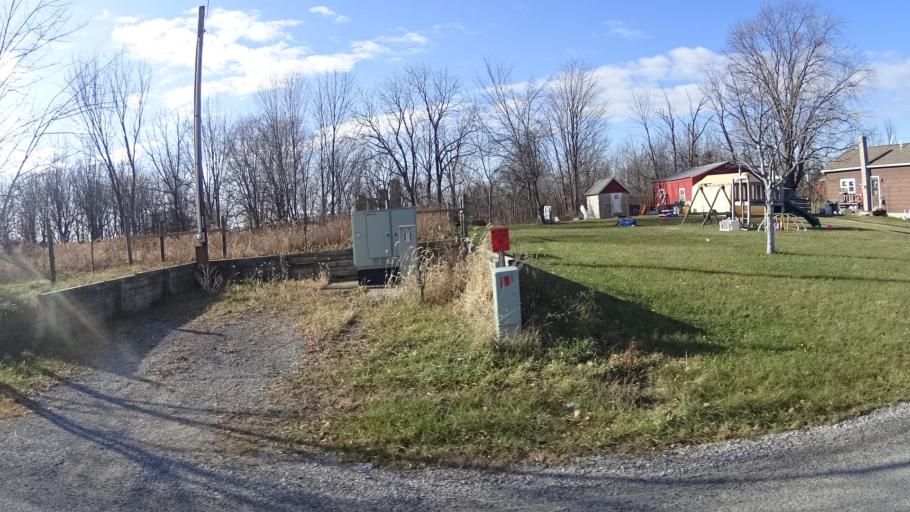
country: US
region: Ohio
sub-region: Lorain County
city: Camden
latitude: 41.2369
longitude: -82.3207
